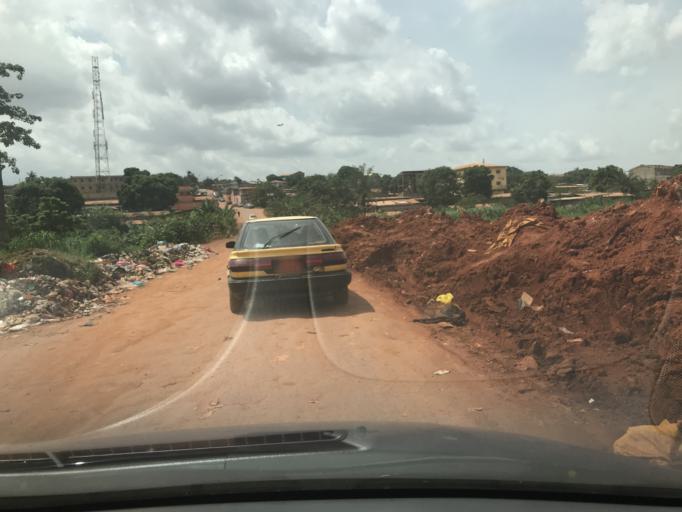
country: CM
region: Centre
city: Yaounde
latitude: 3.8468
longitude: 11.5324
